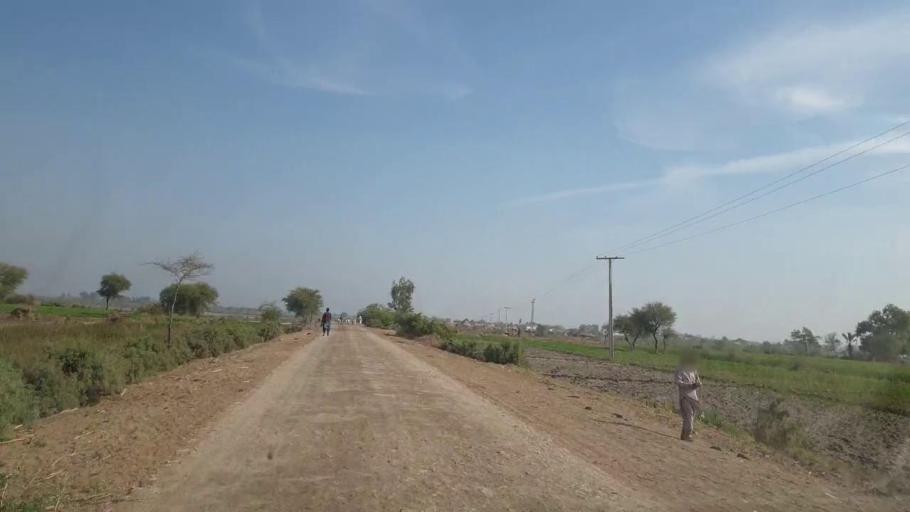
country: PK
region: Sindh
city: Mirpur Khas
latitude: 25.5133
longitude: 69.0956
